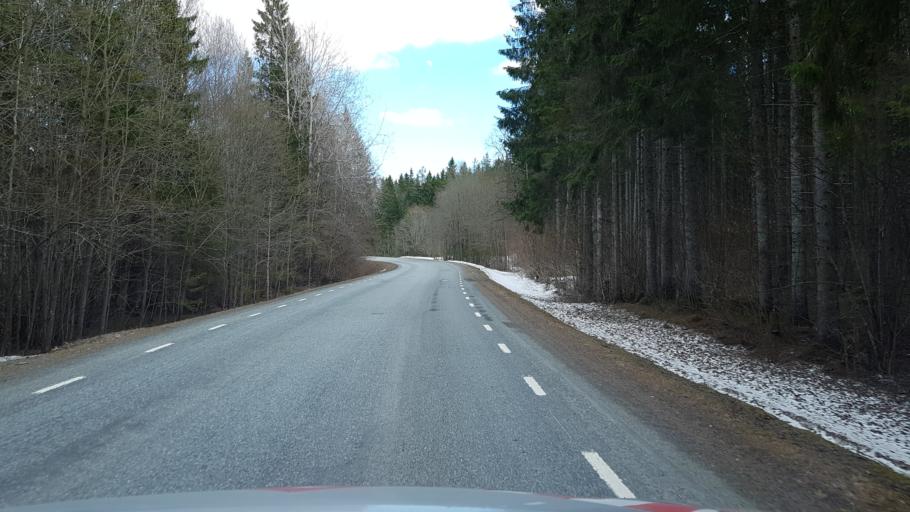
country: EE
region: Laeaene-Virumaa
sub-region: Kadrina vald
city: Kadrina
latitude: 59.2546
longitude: 26.2243
